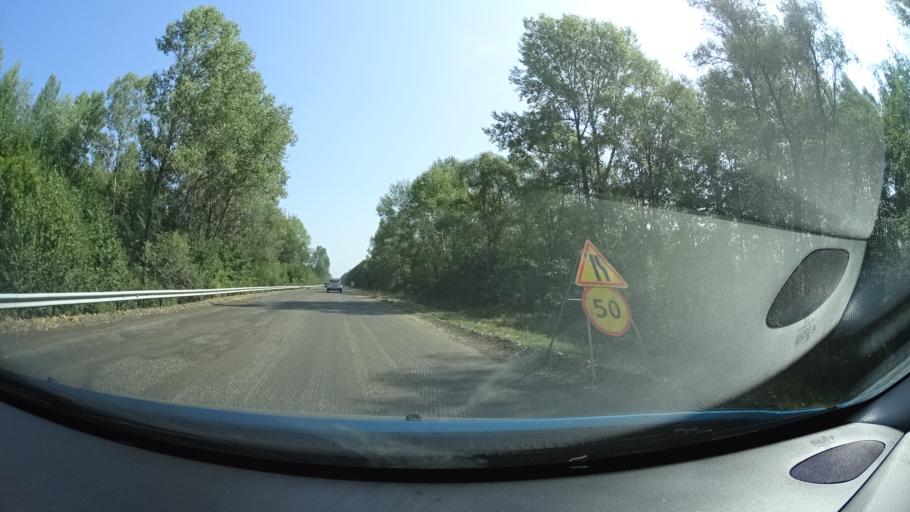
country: RU
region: Bashkortostan
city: Ulukulevo
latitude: 54.4543
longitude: 56.4983
